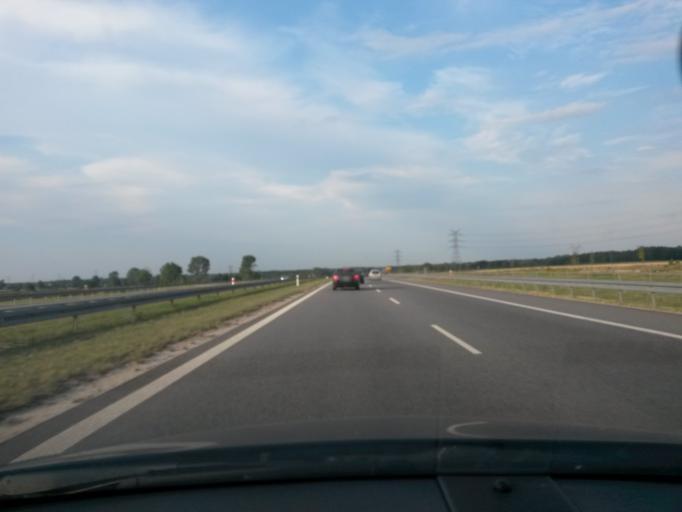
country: PL
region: Lodz Voivodeship
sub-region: Powiat brzezinski
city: Dmosin
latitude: 51.9133
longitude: 19.7507
